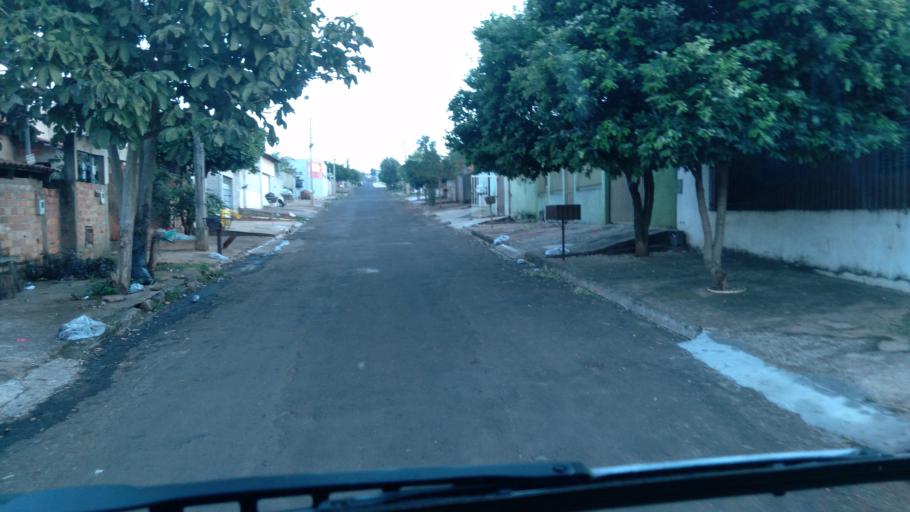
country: BR
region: Goias
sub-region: Mineiros
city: Mineiros
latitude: -17.5745
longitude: -52.5698
